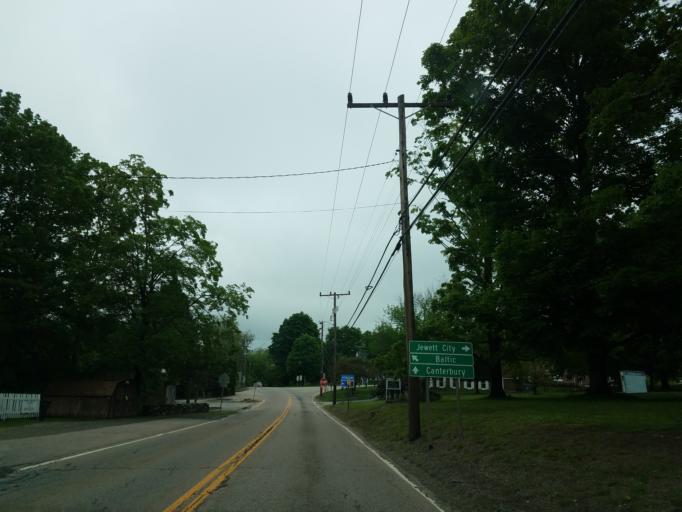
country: US
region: Connecticut
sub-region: New London County
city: Lisbon
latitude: 41.6034
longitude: -72.0178
